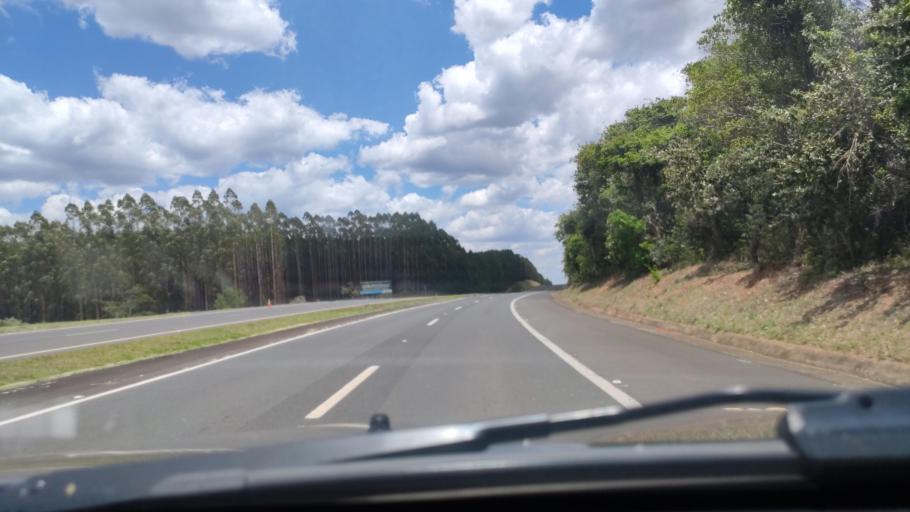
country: BR
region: Sao Paulo
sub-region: Duartina
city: Duartina
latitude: -22.4878
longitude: -49.2428
